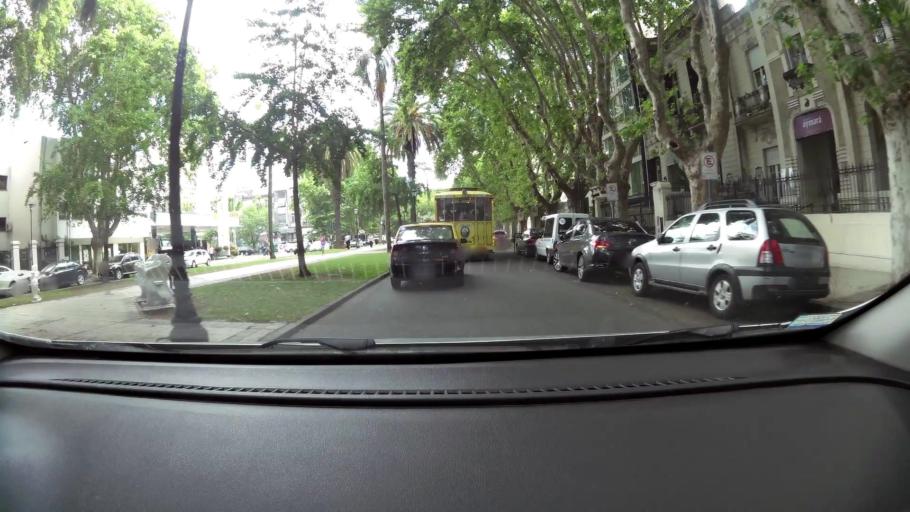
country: AR
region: Santa Fe
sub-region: Departamento de Rosario
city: Rosario
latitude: -32.9507
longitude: -60.6550
